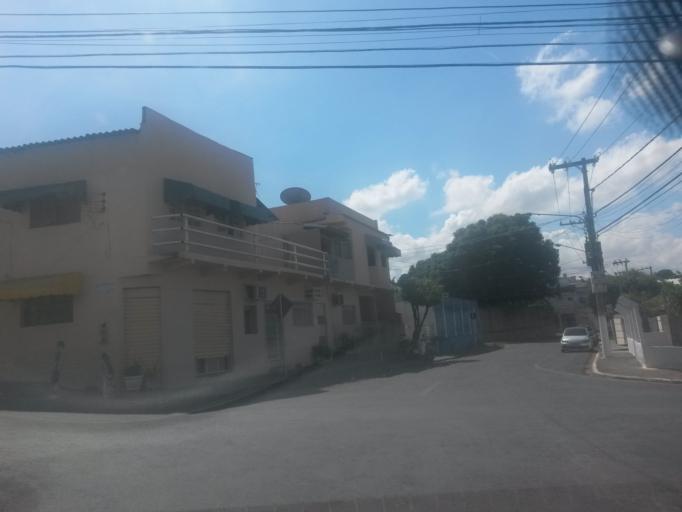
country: BR
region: Mato Grosso
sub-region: Cuiaba
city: Cuiaba
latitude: -15.5962
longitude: -56.0862
